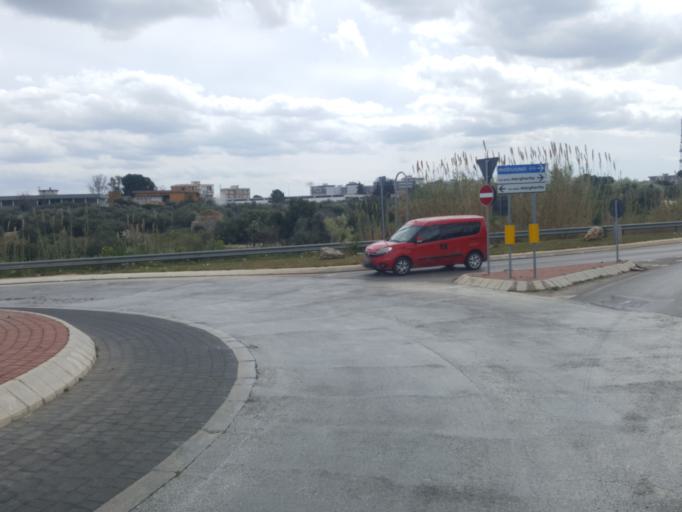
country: IT
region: Apulia
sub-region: Provincia di Bari
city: Modugno
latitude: 41.0975
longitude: 16.7822
